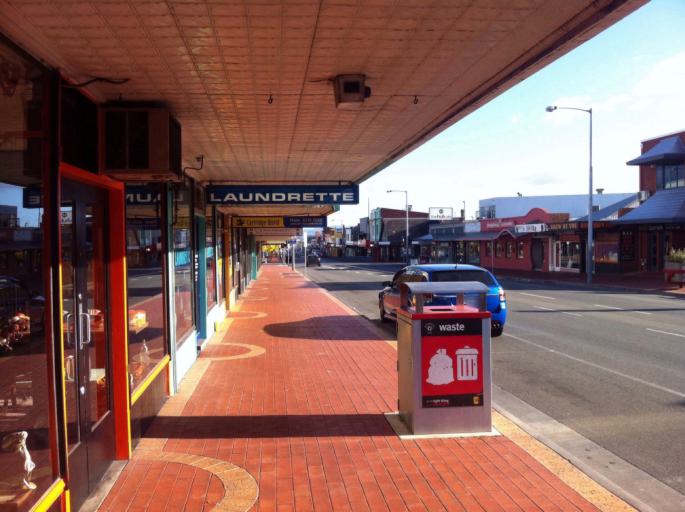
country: AU
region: Tasmania
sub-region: Glenorchy
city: Moonah
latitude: -42.8485
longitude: 147.2964
